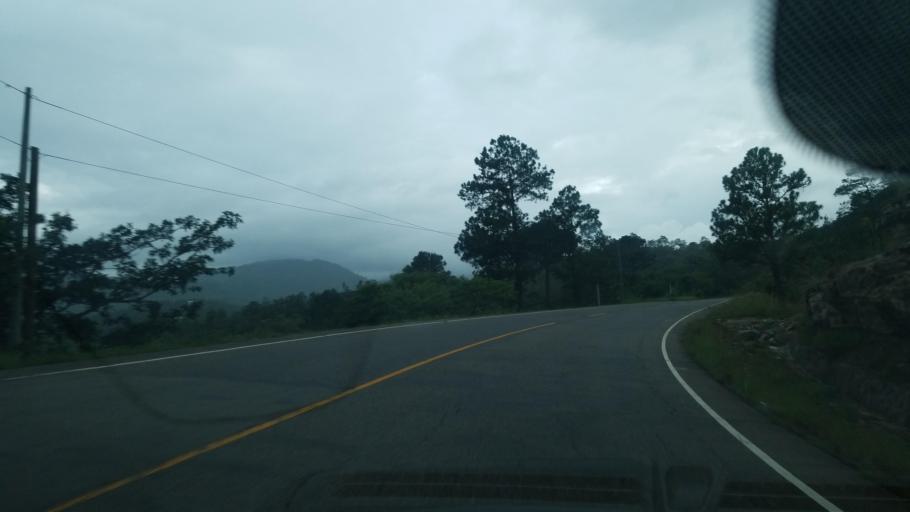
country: HN
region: Ocotepeque
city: Sinuapa
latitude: 14.5222
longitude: -89.2475
